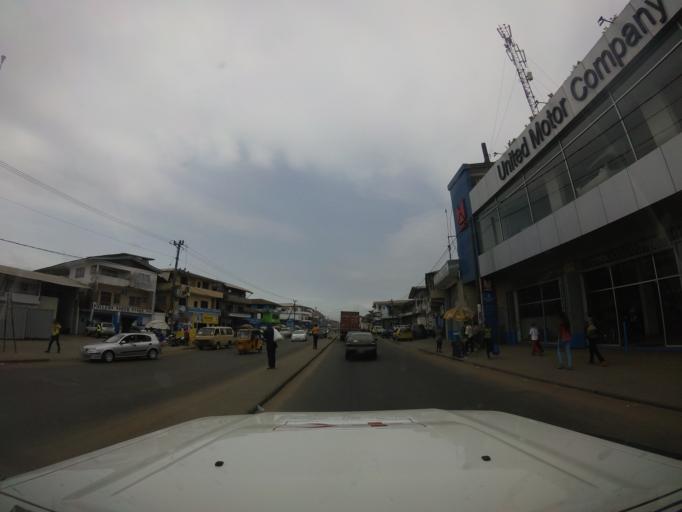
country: LR
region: Montserrado
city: Monrovia
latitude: 6.3234
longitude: -10.8021
